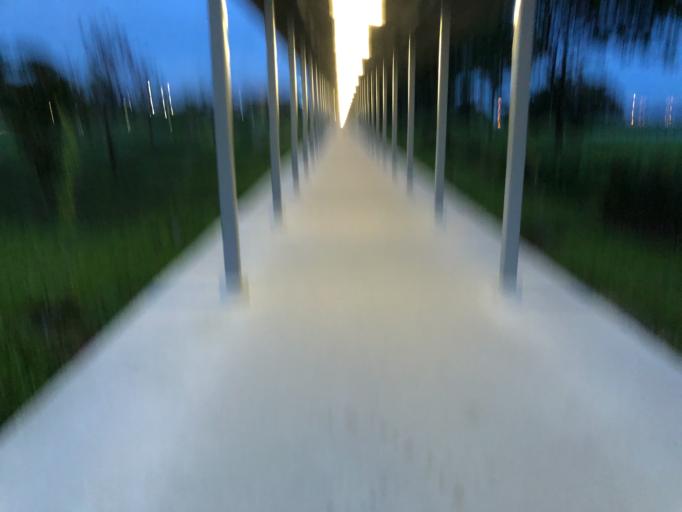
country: SG
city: Singapore
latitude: 1.2688
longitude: 103.8608
